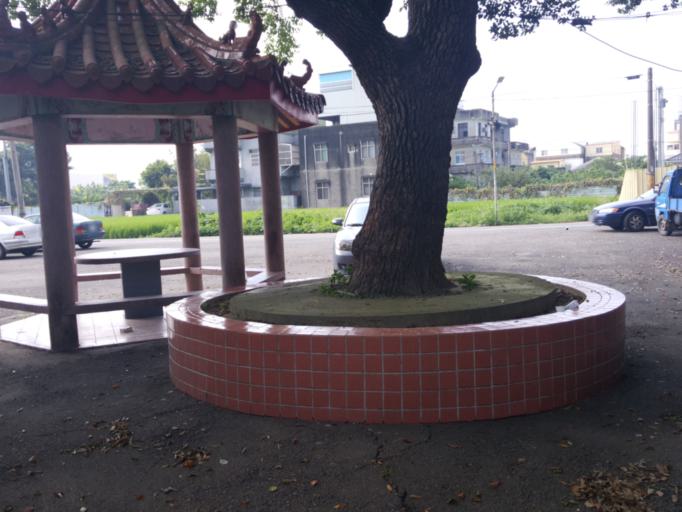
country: TW
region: Taiwan
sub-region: Hsinchu
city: Hsinchu
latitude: 24.6898
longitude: 120.9200
